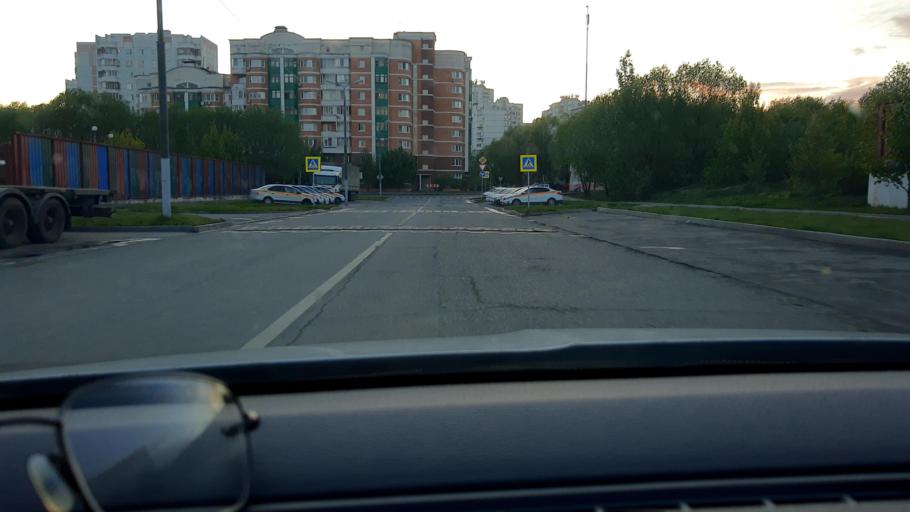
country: RU
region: Moskovskaya
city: Shcherbinka
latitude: 55.5445
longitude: 37.5641
